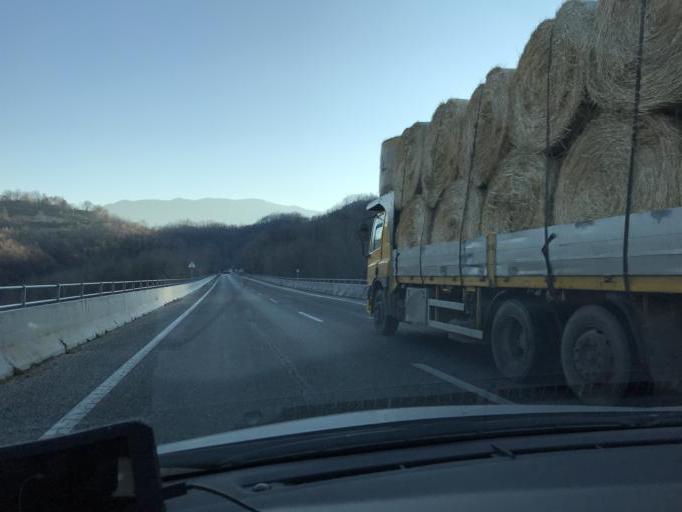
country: IT
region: Latium
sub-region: Provincia di Rieti
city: Fiamignano
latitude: 42.2546
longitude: 13.1421
